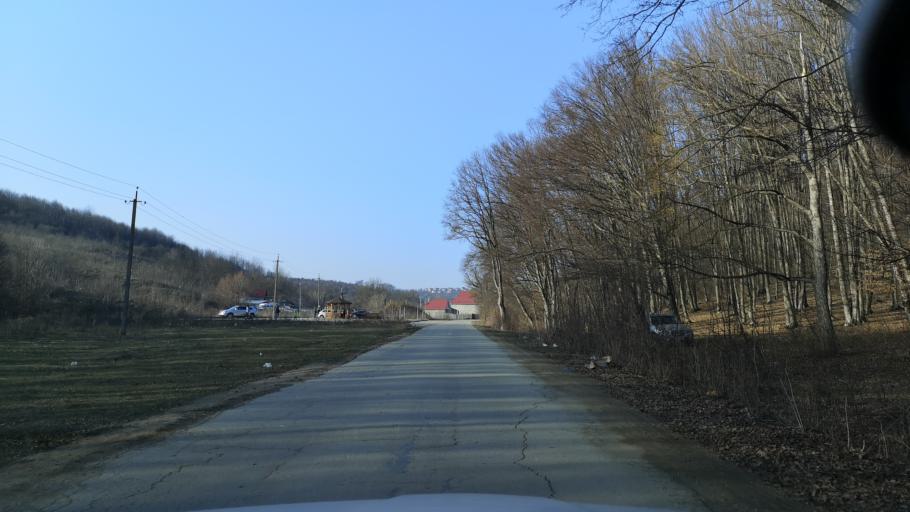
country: MD
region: Nisporeni
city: Nisporeni
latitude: 47.0867
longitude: 28.3196
